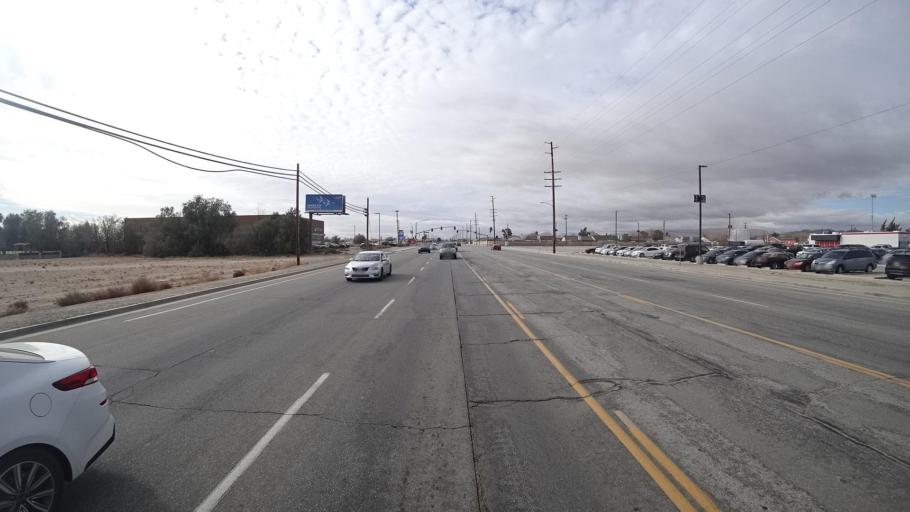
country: US
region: California
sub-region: Kern County
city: Rosamond
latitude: 34.8640
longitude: -118.1832
